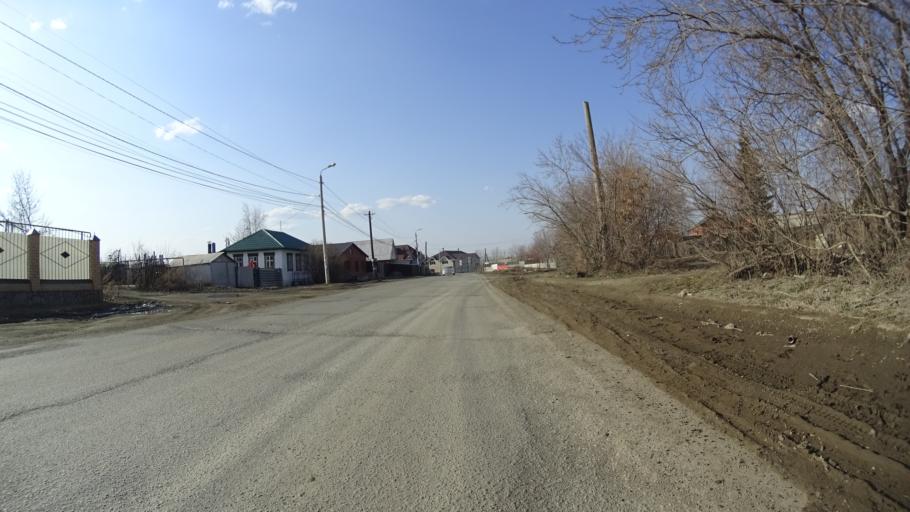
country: RU
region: Chelyabinsk
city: Novosineglazovskiy
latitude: 55.1098
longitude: 61.3332
